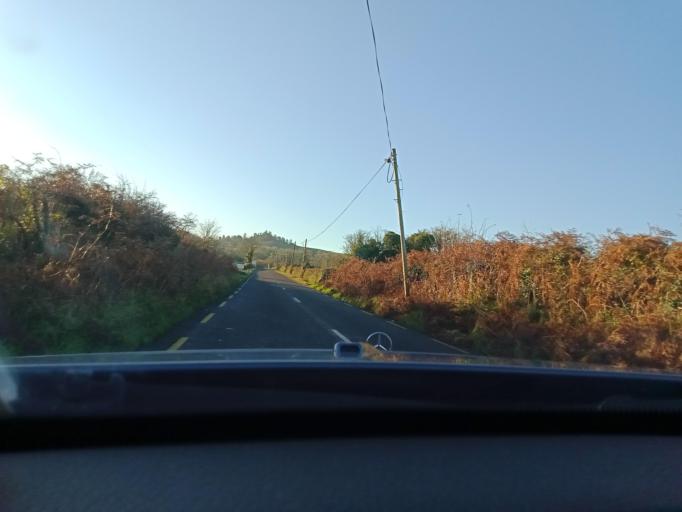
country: IE
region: Leinster
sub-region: Kilkenny
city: Callan
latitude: 52.4705
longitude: -7.3948
